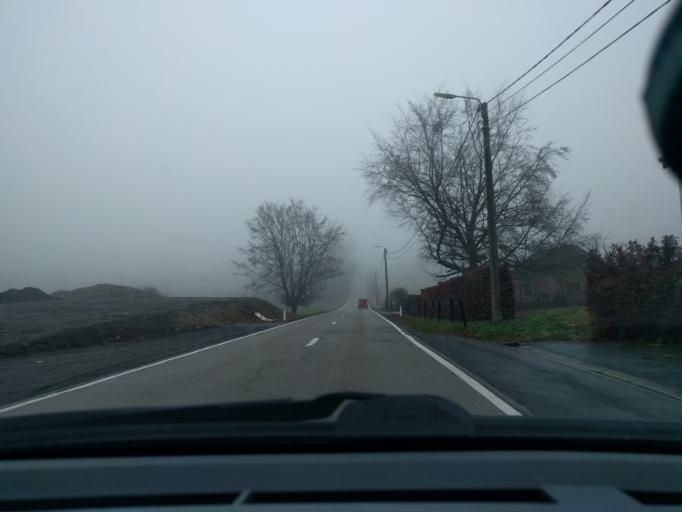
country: BE
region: Wallonia
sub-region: Province du Luxembourg
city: Gouvy
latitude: 50.1914
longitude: 5.9204
